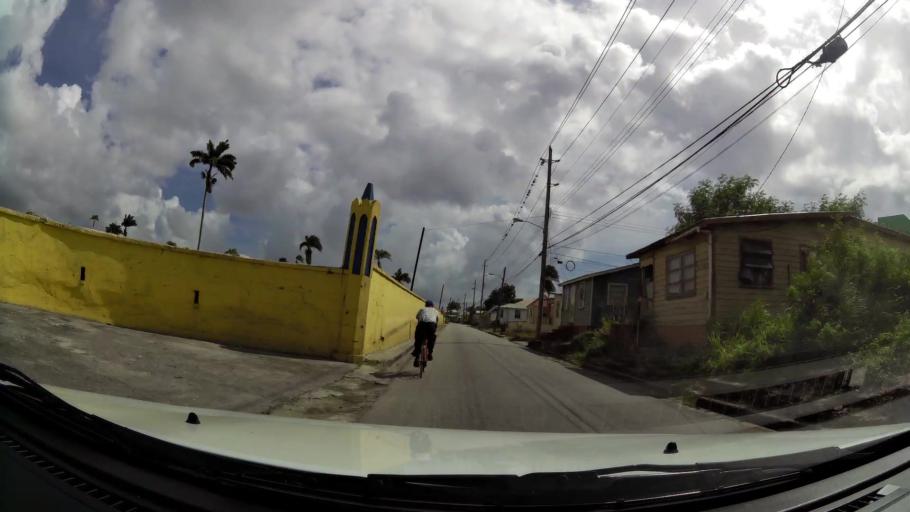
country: BB
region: Saint Michael
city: Bridgetown
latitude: 13.1098
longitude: -59.6225
